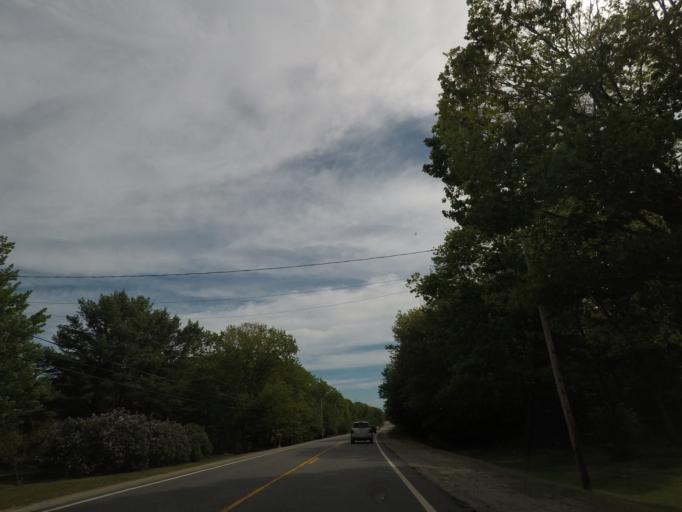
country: US
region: Maine
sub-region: Sagadahoc County
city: Richmond
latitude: 44.1085
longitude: -69.7822
